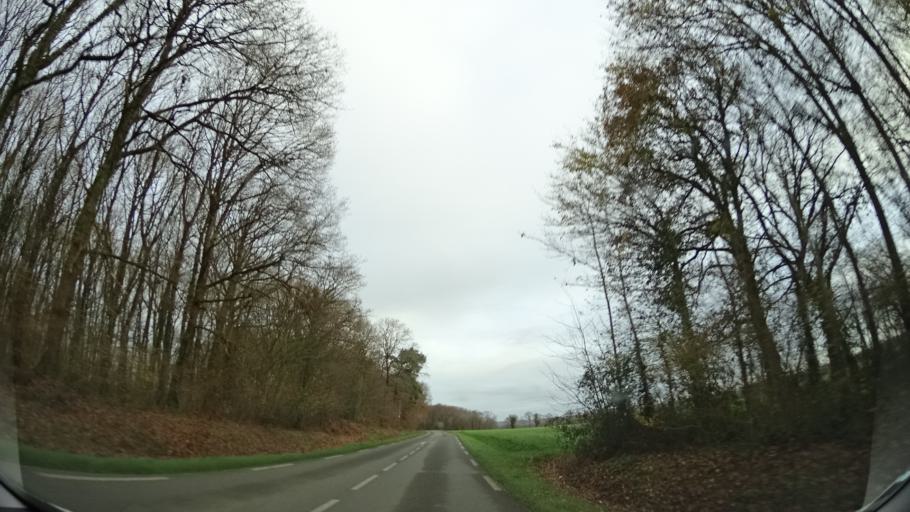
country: FR
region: Brittany
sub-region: Departement des Cotes-d'Armor
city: Evran
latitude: 48.3542
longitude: -1.9686
